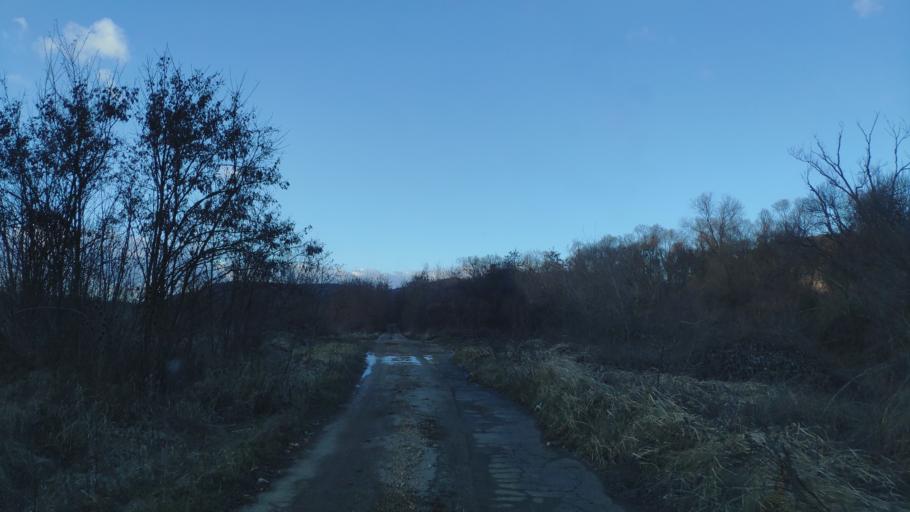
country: HU
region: Borsod-Abauj-Zemplen
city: Tolcsva
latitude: 48.2842
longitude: 21.4873
